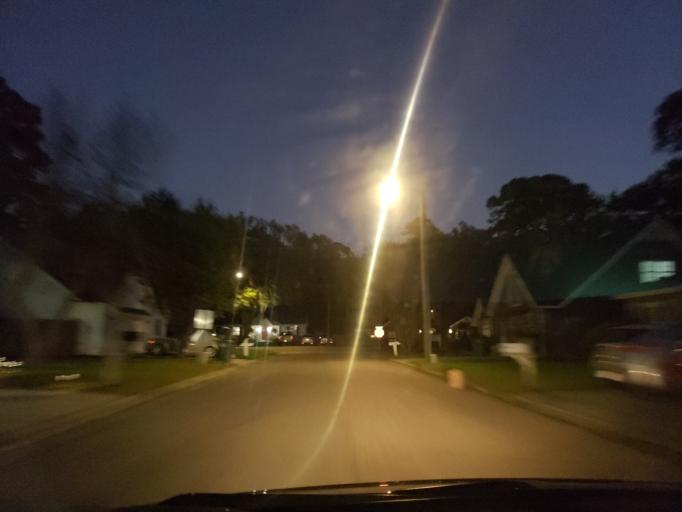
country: US
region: Georgia
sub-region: Chatham County
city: Isle of Hope
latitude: 31.9932
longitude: -81.0667
